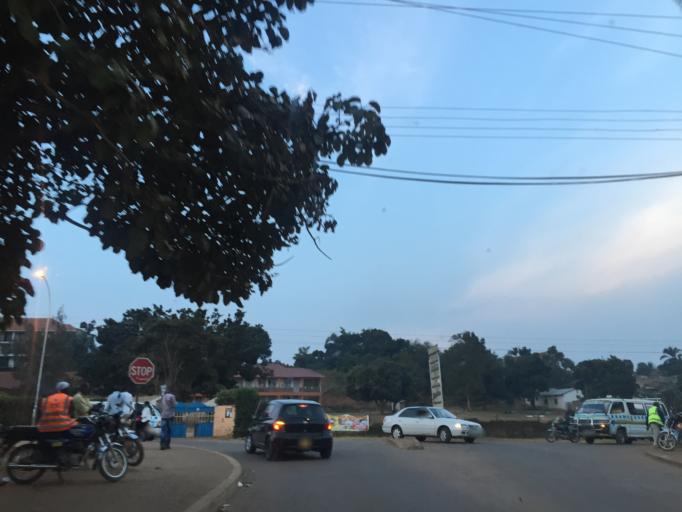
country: UG
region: Central Region
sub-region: Kampala District
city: Kampala
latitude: 0.2578
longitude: 32.6281
